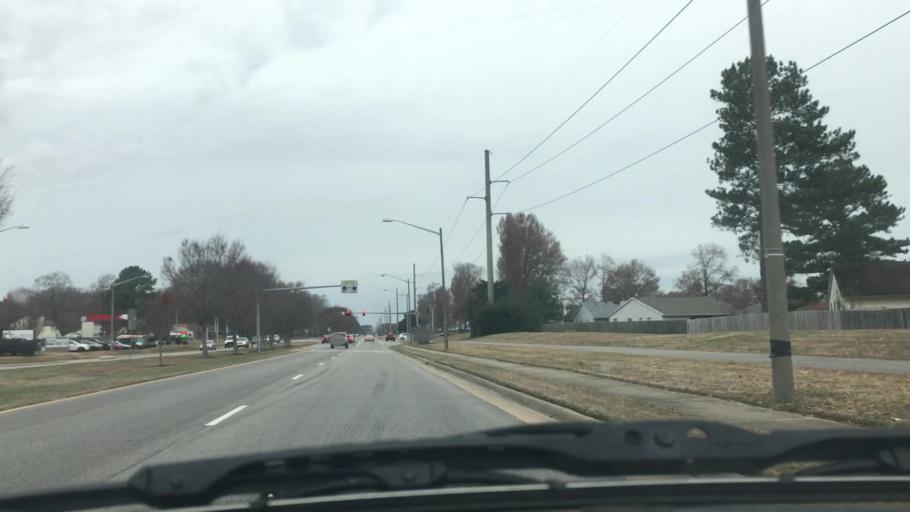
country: US
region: Virginia
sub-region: City of Virginia Beach
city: Virginia Beach
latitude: 36.8008
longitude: -76.1106
